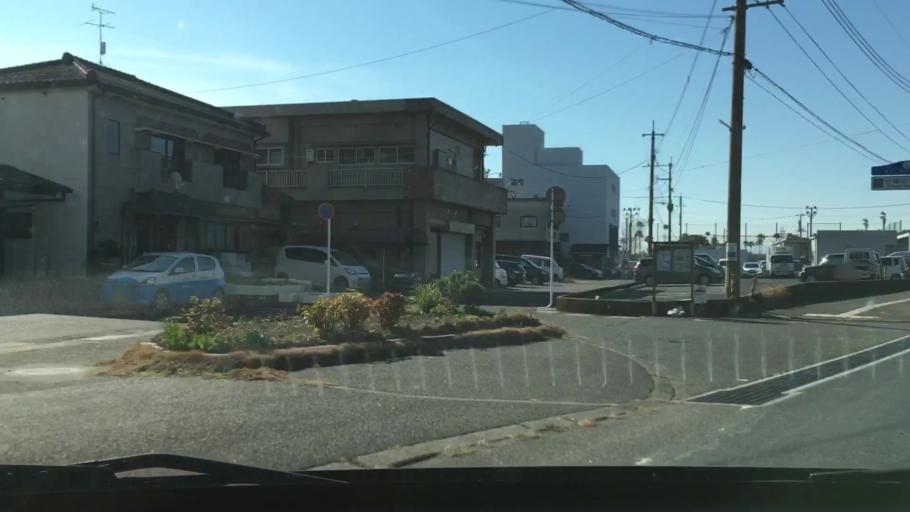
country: JP
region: Kagoshima
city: Kagoshima-shi
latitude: 31.6061
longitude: 130.5728
